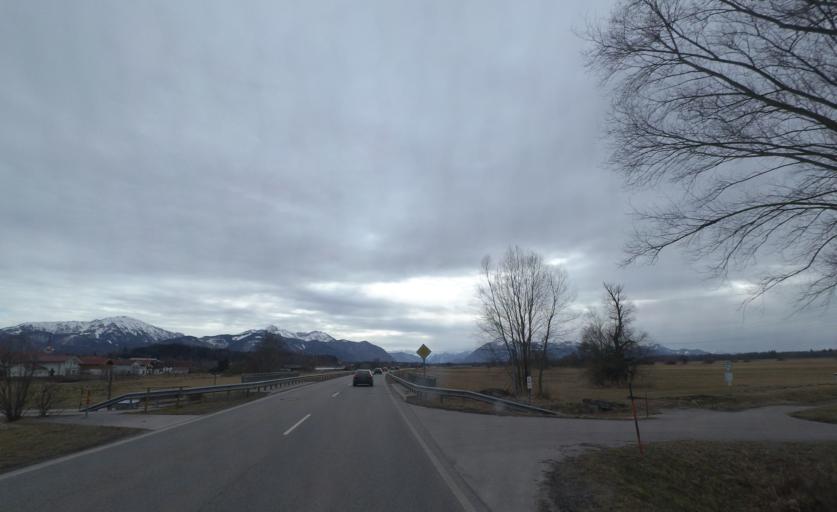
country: DE
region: Bavaria
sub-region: Upper Bavaria
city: Grabenstatt
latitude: 47.8473
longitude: 12.5397
